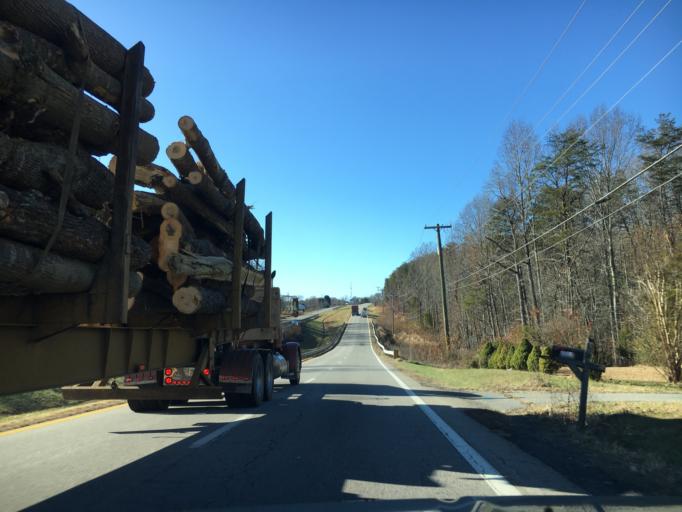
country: US
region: Virginia
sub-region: Henry County
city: Chatmoss
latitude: 36.6238
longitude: -79.6168
